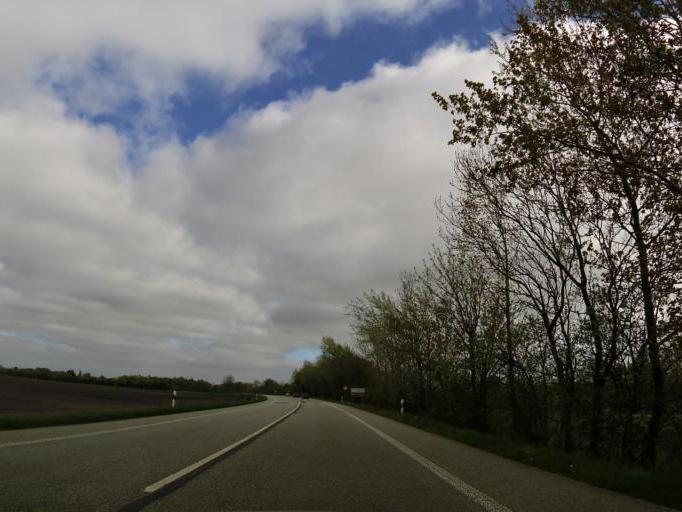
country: DE
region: Schleswig-Holstein
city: Risum-Lindholm
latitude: 54.7739
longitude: 8.8572
